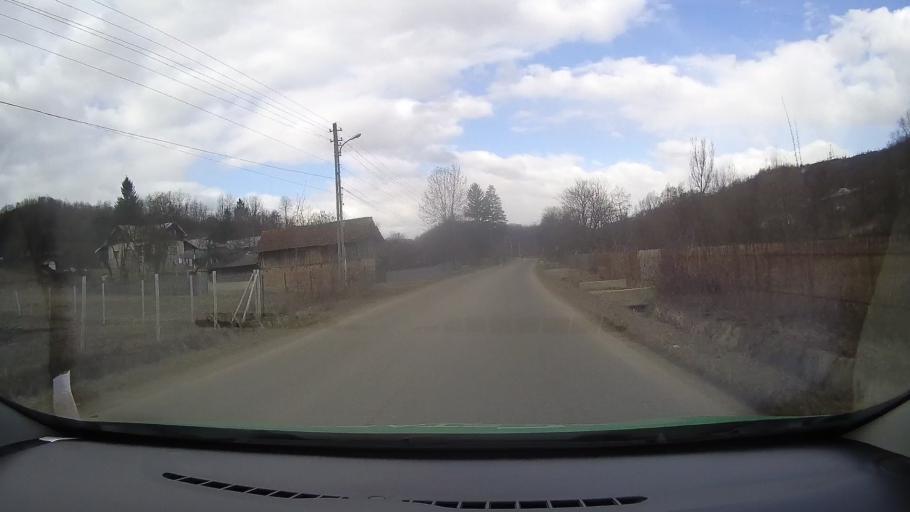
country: RO
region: Dambovita
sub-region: Comuna Valea Lunga
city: Valea Lunga-Cricov
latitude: 45.0642
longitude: 25.5594
